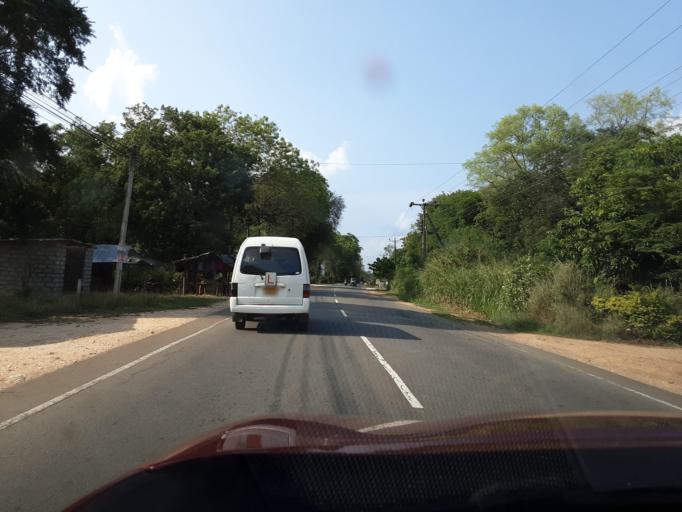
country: LK
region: Uva
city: Haputale
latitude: 6.5884
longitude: 81.1414
